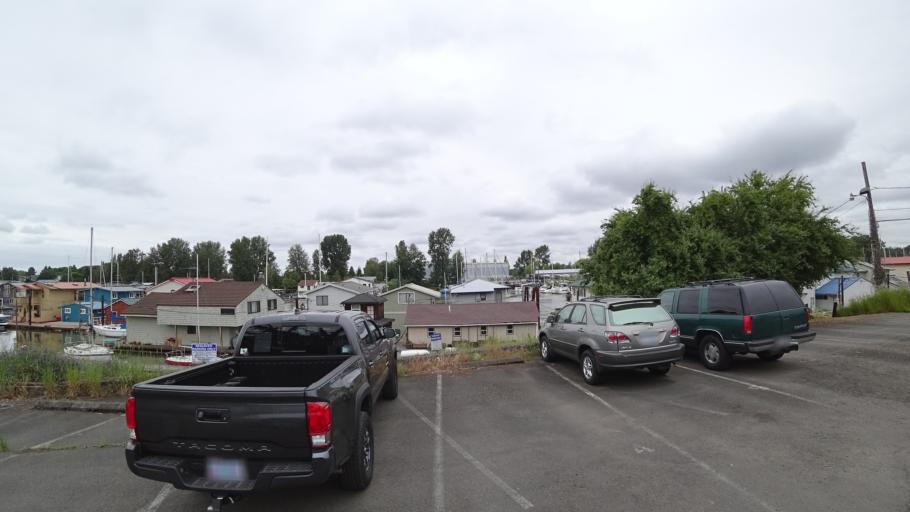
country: US
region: Washington
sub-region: Clark County
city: Vancouver
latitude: 45.6025
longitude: -122.6660
